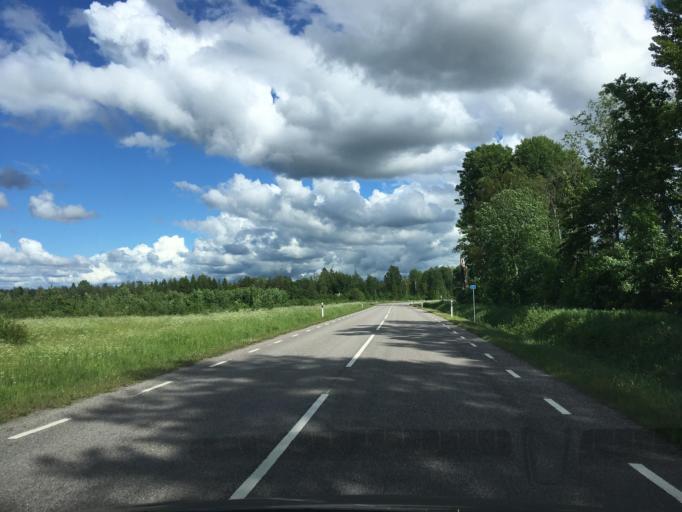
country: EE
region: Paernumaa
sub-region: Halinga vald
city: Parnu-Jaagupi
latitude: 58.6709
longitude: 24.6320
